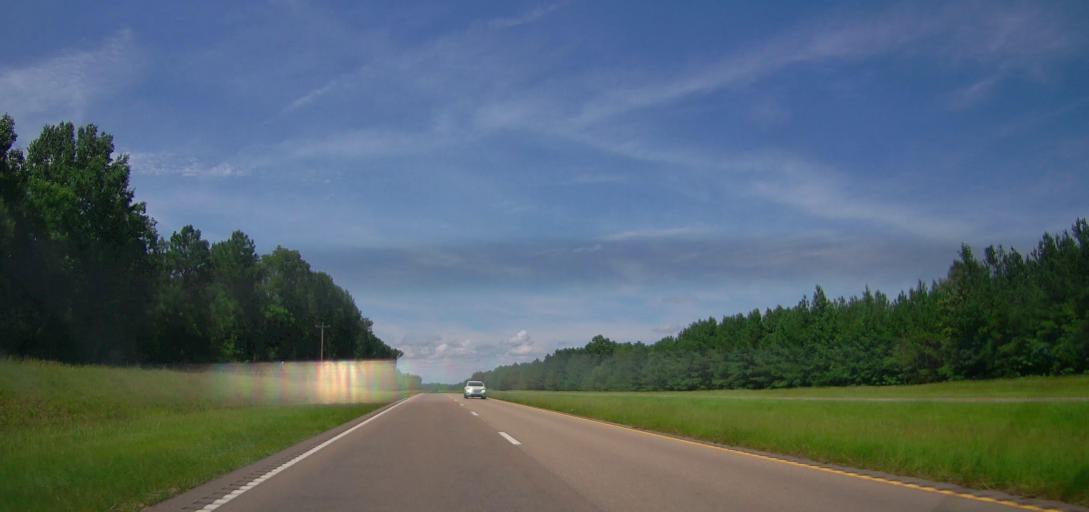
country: US
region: Mississippi
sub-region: Monroe County
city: Aberdeen
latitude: 33.9178
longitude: -88.5963
